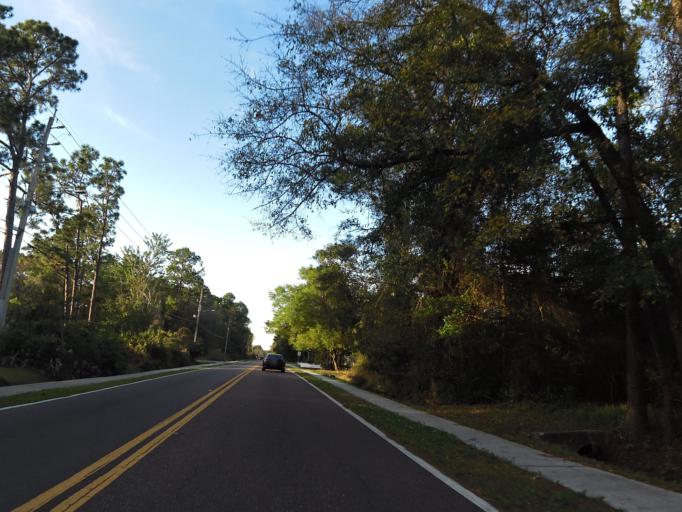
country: US
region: Florida
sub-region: Duval County
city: Jacksonville
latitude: 30.4318
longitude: -81.6716
